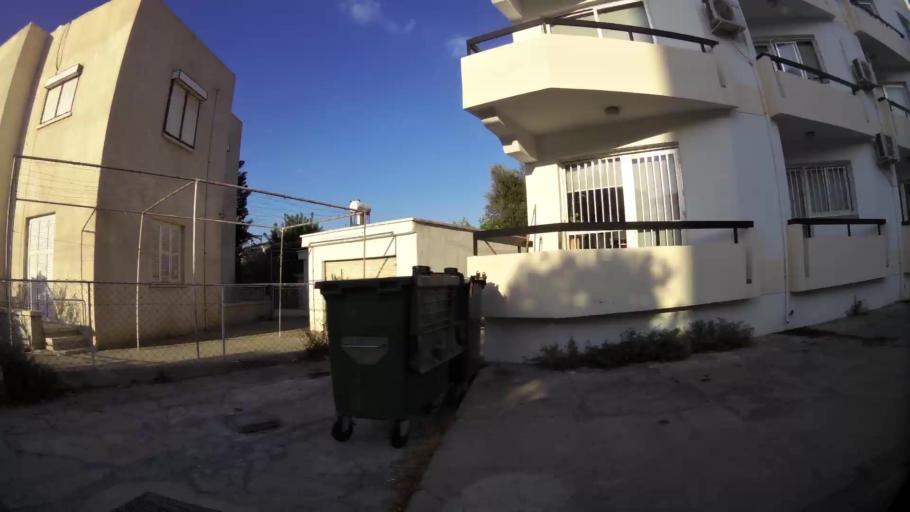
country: CY
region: Lefkosia
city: Nicosia
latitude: 35.1888
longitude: 33.3550
